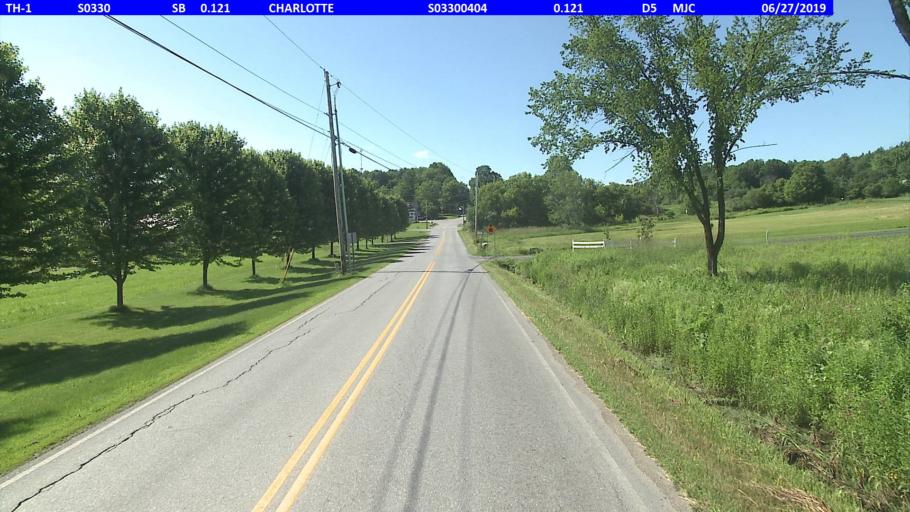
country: US
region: Vermont
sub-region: Chittenden County
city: Hinesburg
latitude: 44.3214
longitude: -73.1895
